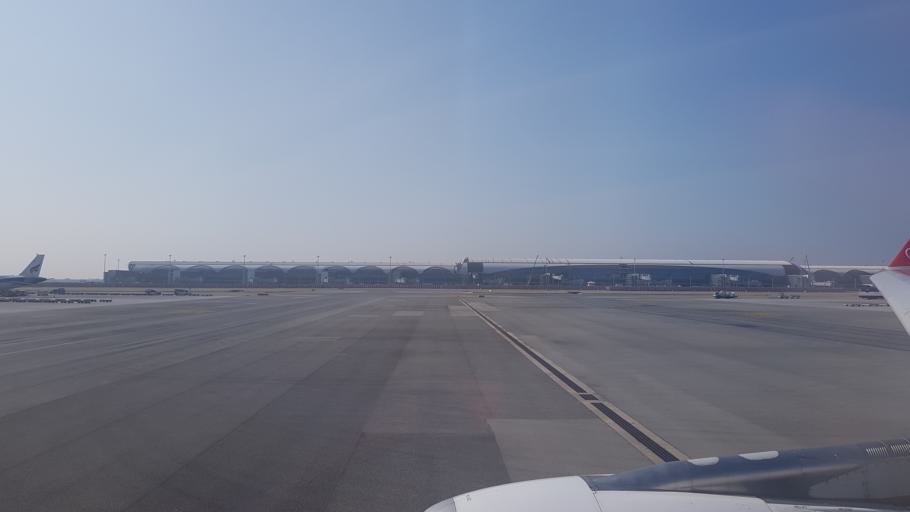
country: TH
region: Bangkok
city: Lat Krabang
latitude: 13.6889
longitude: 100.7517
